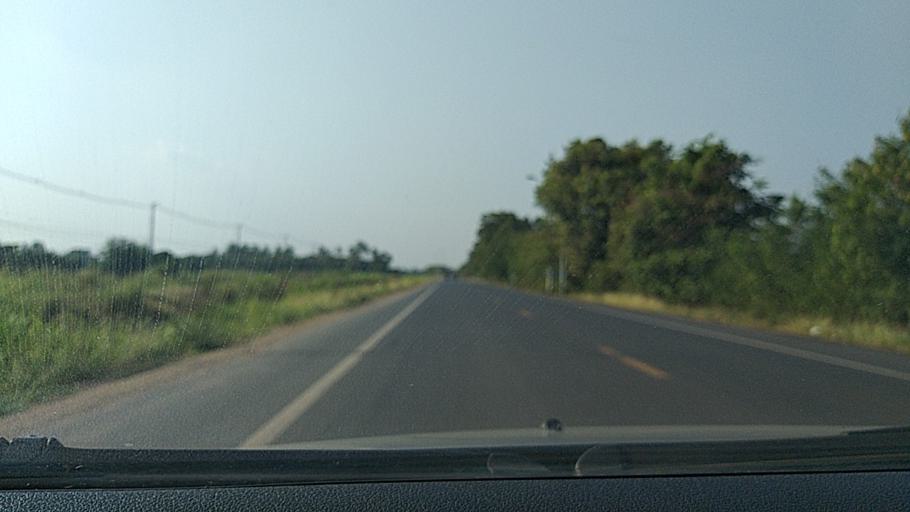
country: TH
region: Sing Buri
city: Phrom Buri
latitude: 14.8151
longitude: 100.4342
